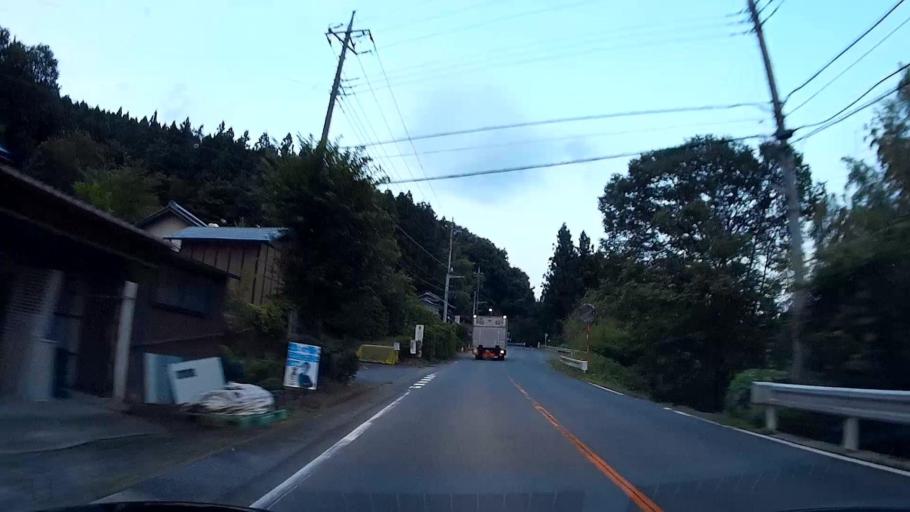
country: JP
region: Gunma
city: Annaka
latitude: 36.3890
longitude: 138.8365
